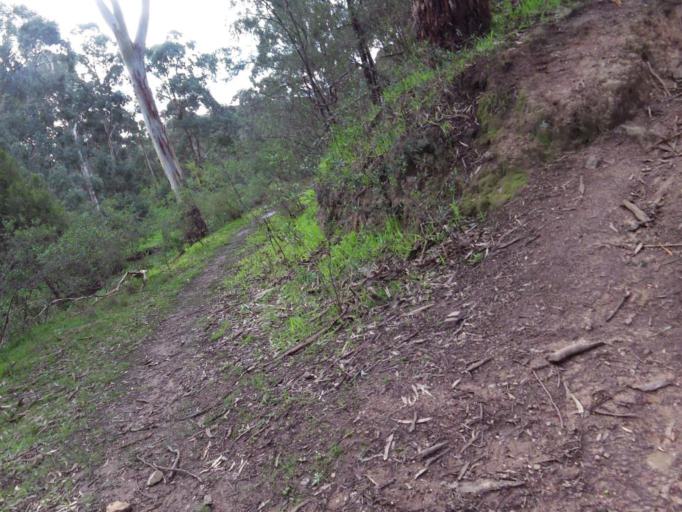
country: AU
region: Victoria
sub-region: Whittlesea
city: Mill Park
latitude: -37.6716
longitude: 145.0867
